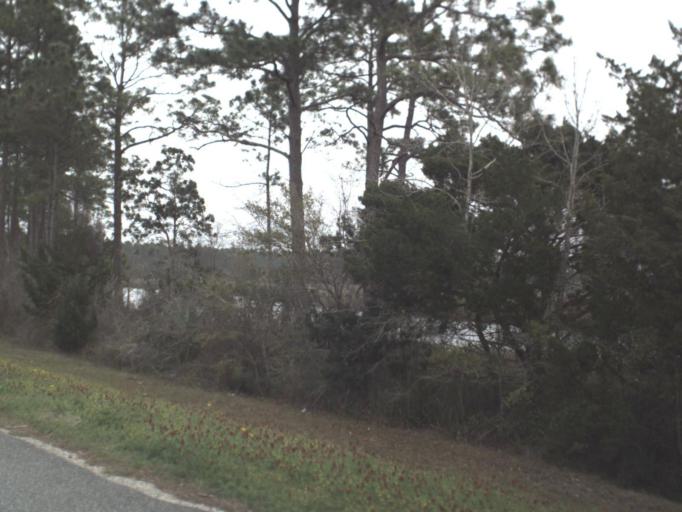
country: US
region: Florida
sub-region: Franklin County
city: Eastpoint
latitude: 29.8242
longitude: -84.9025
